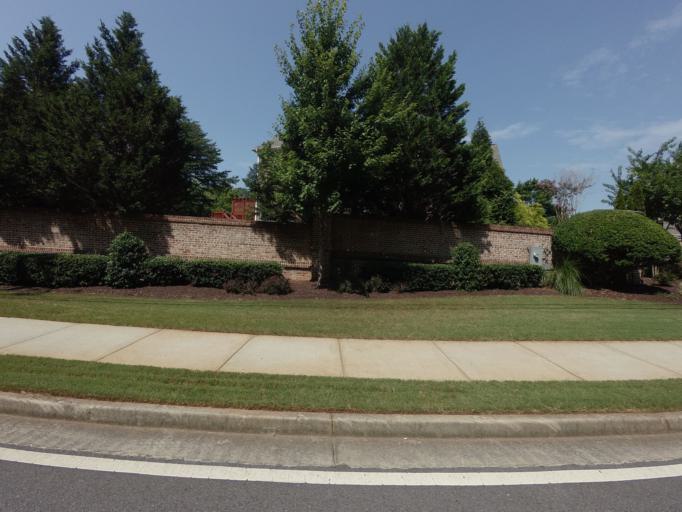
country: US
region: Georgia
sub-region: Fulton County
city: Alpharetta
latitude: 34.0295
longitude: -84.2699
